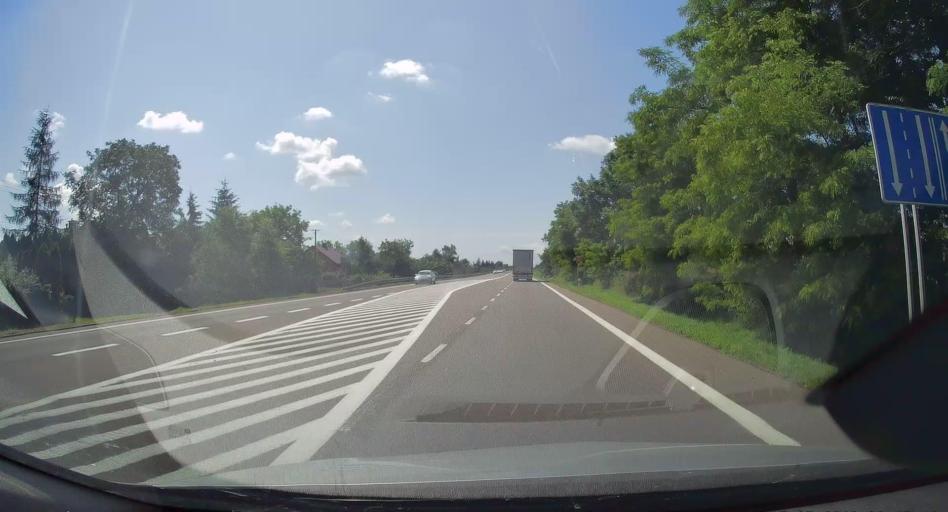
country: PL
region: Subcarpathian Voivodeship
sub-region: Powiat przemyski
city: Orly
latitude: 49.8987
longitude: 22.8164
